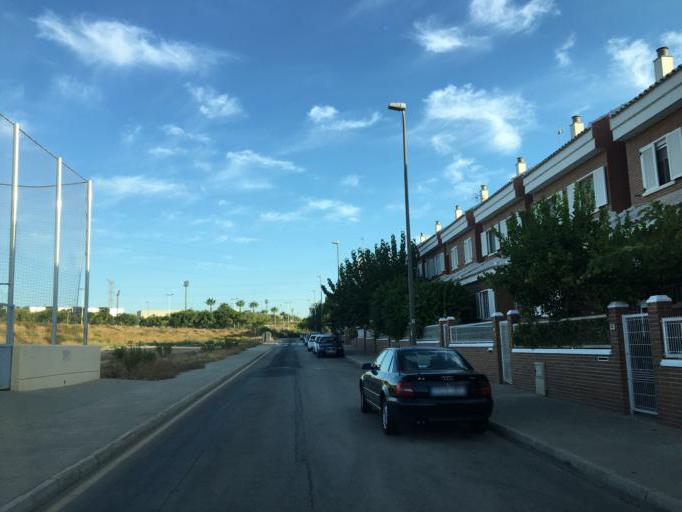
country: ES
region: Murcia
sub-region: Murcia
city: Murcia
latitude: 38.0130
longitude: -1.1646
